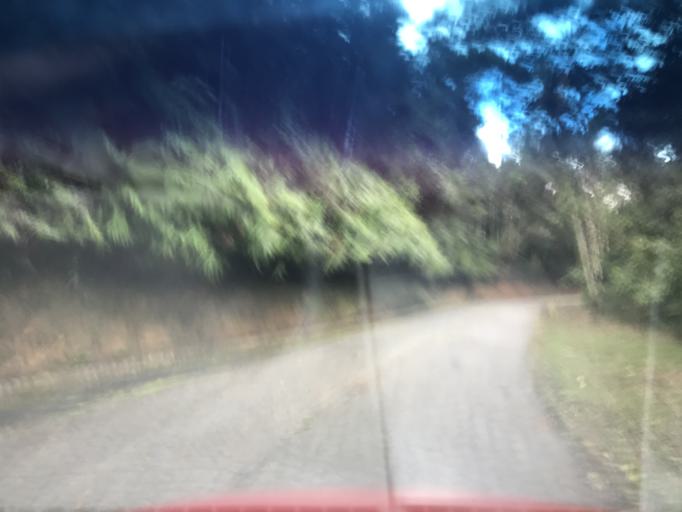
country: BR
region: Bahia
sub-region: Gandu
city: Gandu
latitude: -13.9059
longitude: -39.4617
